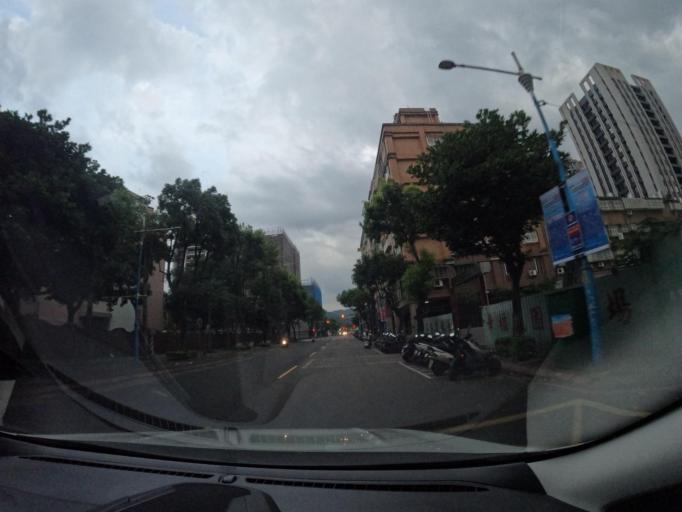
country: TW
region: Taipei
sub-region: Taipei
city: Banqiao
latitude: 24.9815
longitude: 121.4509
